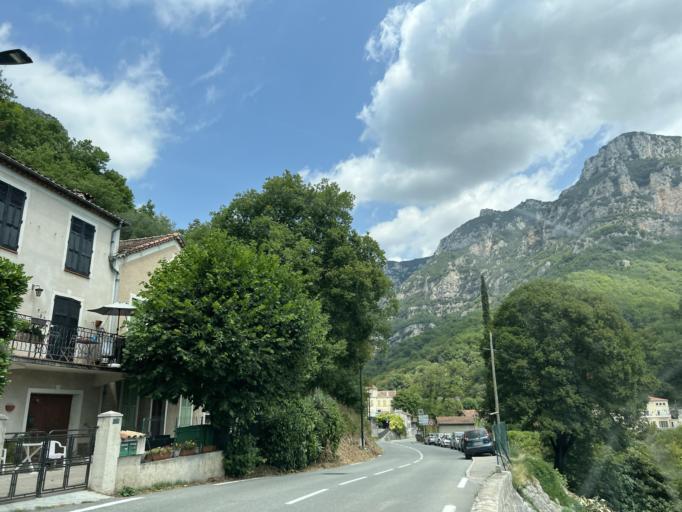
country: FR
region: Provence-Alpes-Cote d'Azur
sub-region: Departement des Alpes-Maritimes
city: Le Rouret
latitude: 43.7182
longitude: 6.9899
